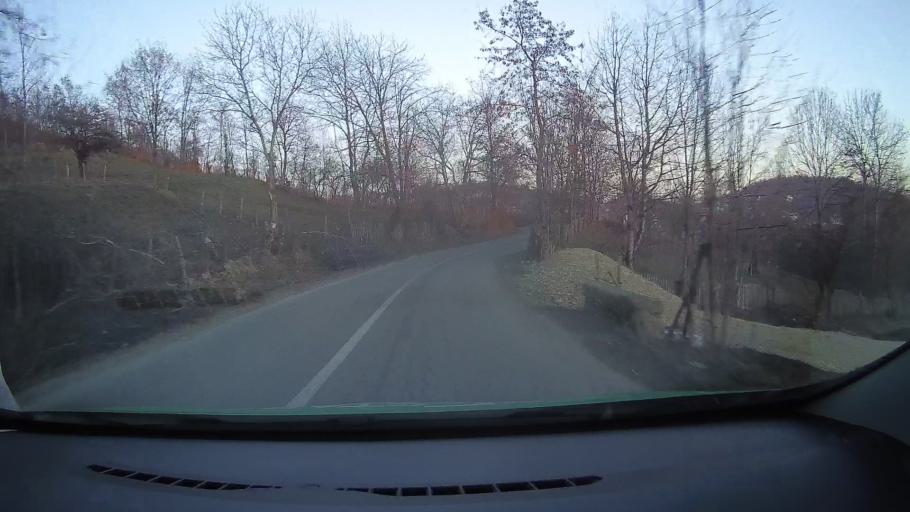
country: RO
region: Prahova
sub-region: Comuna Comarnic
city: Poiana
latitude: 45.2601
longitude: 25.6559
